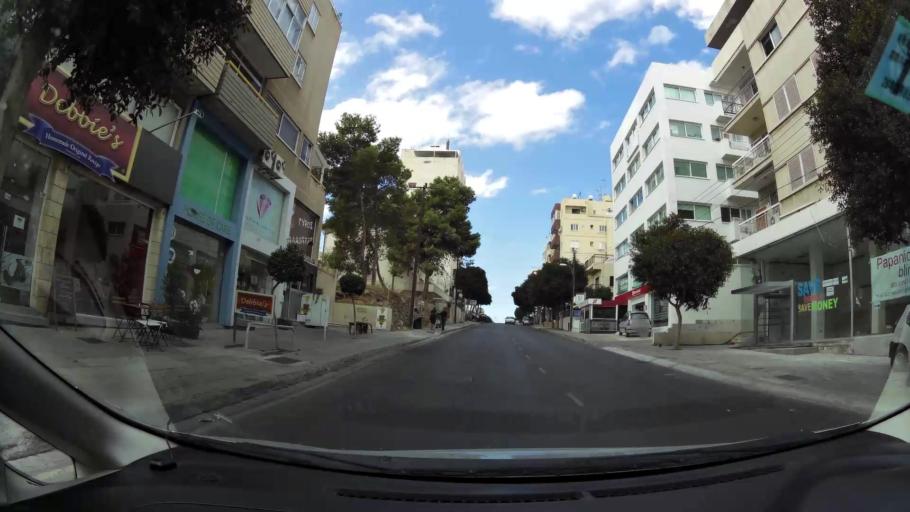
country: CY
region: Lefkosia
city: Nicosia
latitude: 35.1576
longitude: 33.3666
